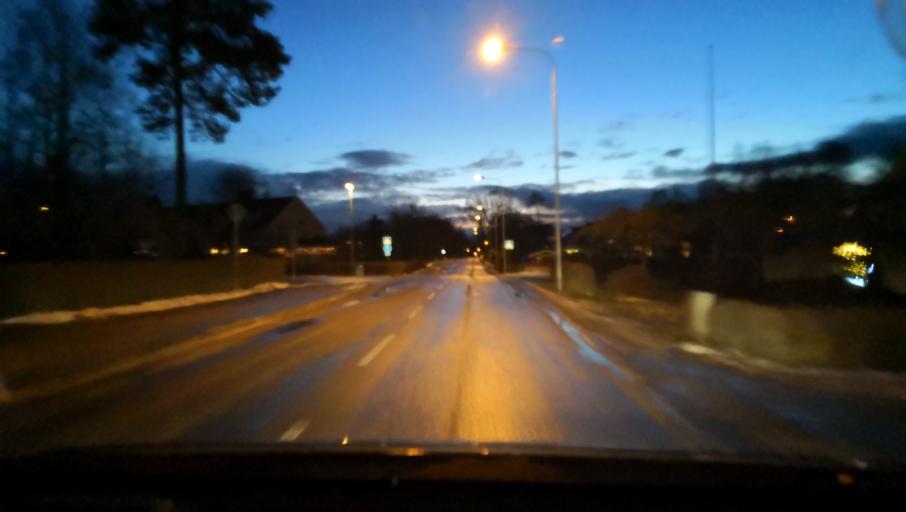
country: SE
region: Vaestmanland
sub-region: Vasteras
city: Skultuna
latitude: 59.7241
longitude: 16.4307
